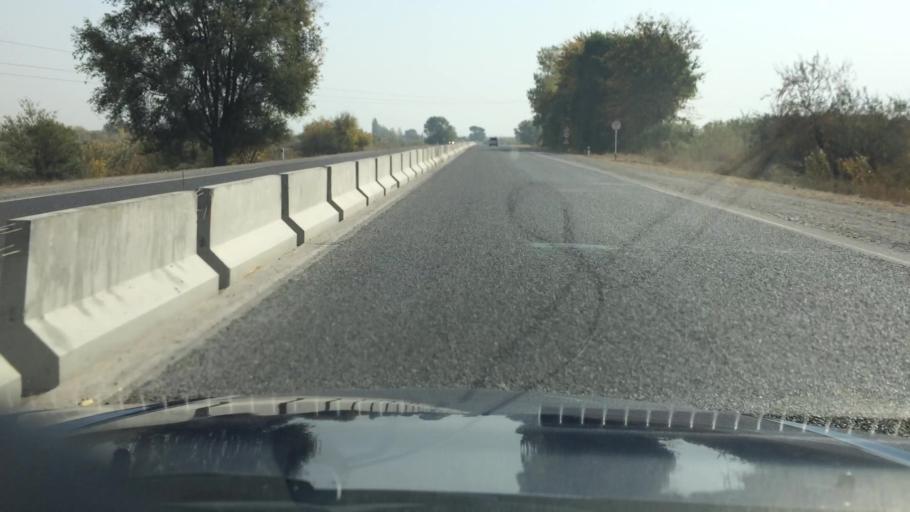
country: KG
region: Chuy
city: Kant
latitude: 42.9623
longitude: 74.9184
